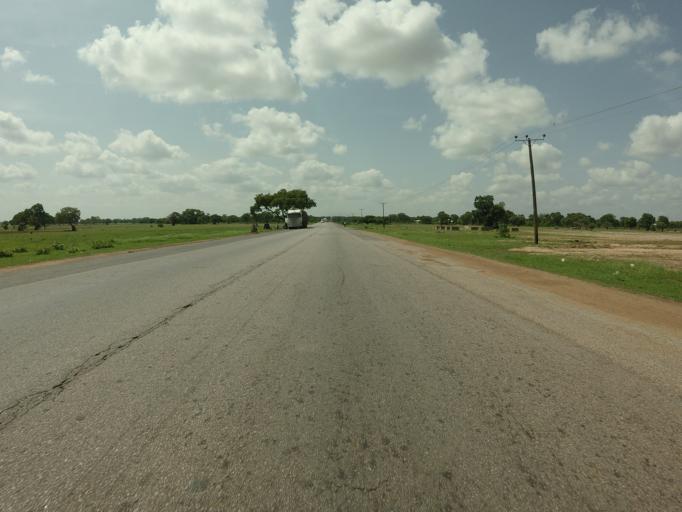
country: GH
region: Northern
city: Savelugu
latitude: 9.5571
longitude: -0.8368
